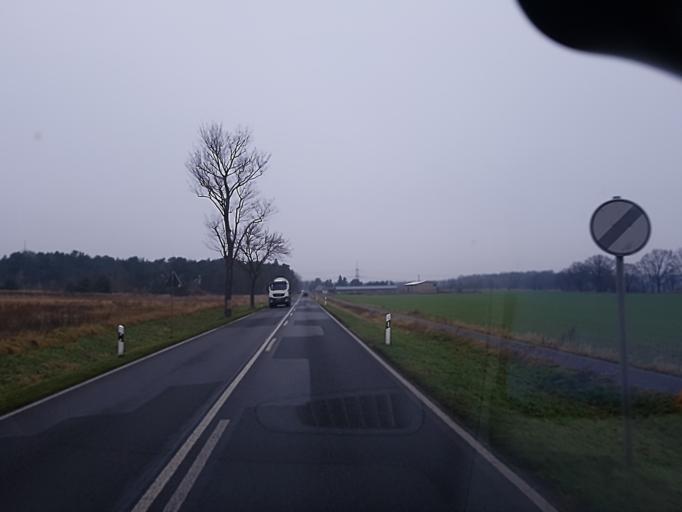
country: DE
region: Brandenburg
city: Lubbenau
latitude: 51.8774
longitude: 13.9100
